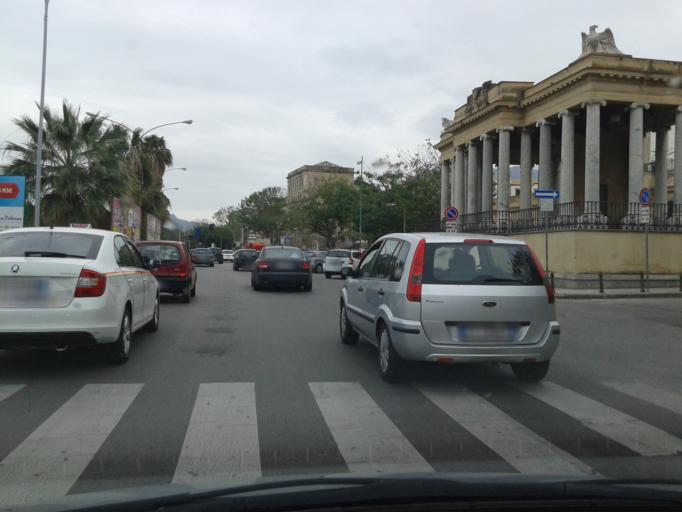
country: IT
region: Sicily
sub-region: Palermo
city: Palermo
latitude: 38.1177
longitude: 13.3729
